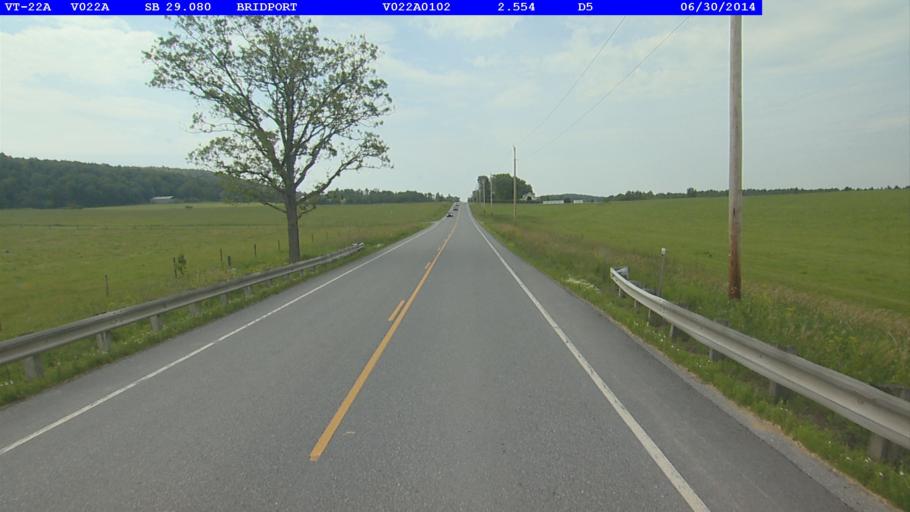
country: US
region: Vermont
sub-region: Addison County
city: Middlebury (village)
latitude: 43.9771
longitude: -73.3118
